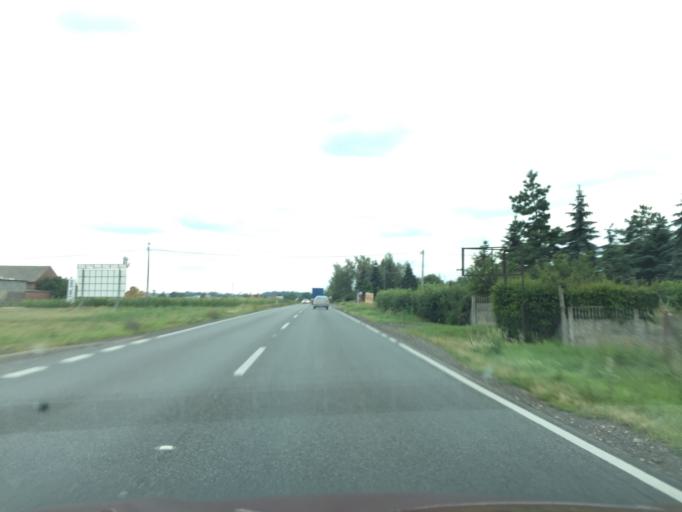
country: PL
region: Greater Poland Voivodeship
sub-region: Kalisz
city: Kalisz
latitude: 51.8337
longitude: 18.0953
